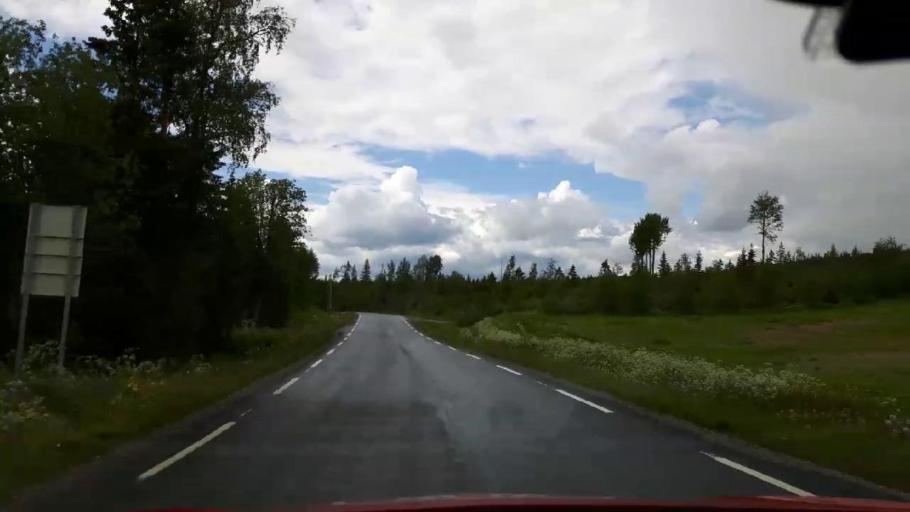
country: NO
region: Nord-Trondelag
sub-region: Lierne
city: Sandvika
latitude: 64.0980
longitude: 14.0334
